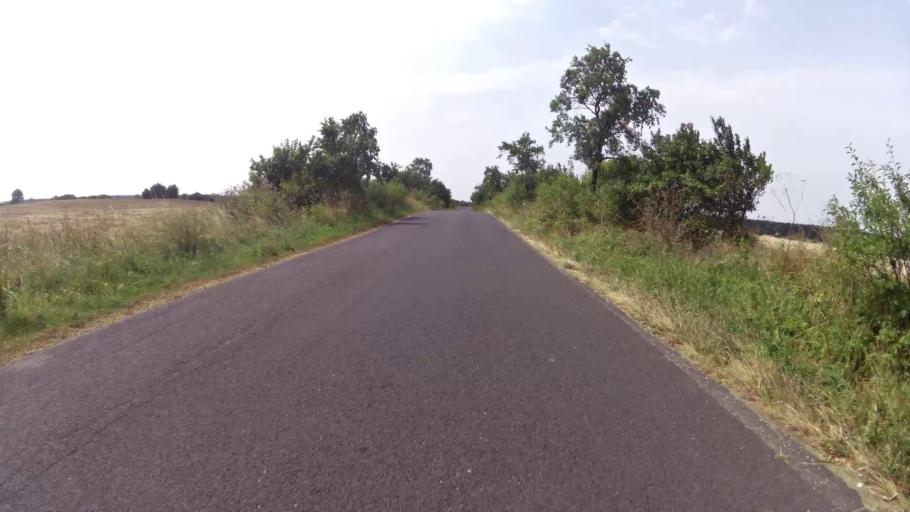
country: PL
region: West Pomeranian Voivodeship
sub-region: Powiat gryfinski
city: Moryn
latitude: 52.8625
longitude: 14.4416
